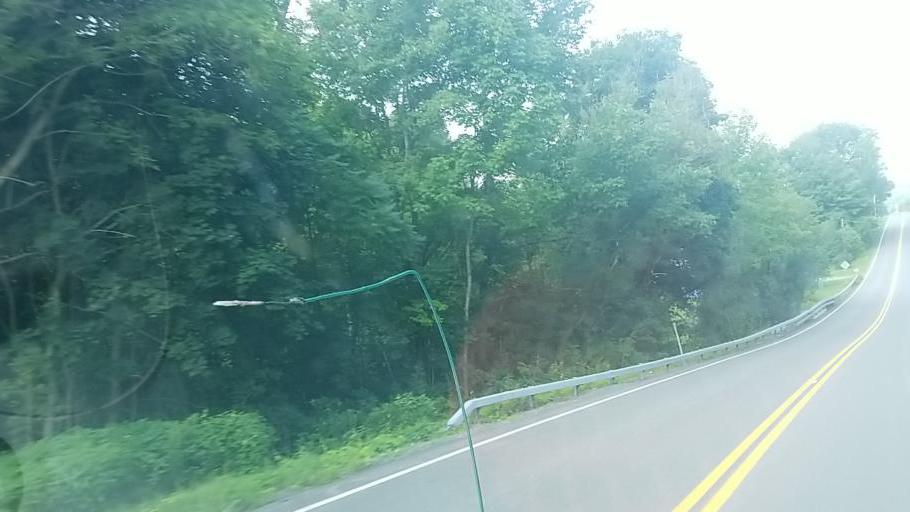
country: US
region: New York
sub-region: Fulton County
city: Gloversville
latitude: 43.1039
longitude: -74.2793
